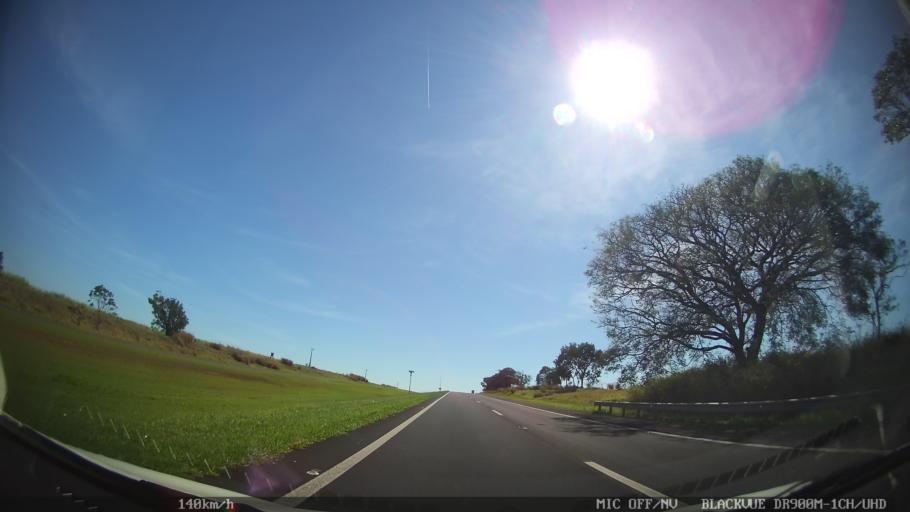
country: BR
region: Sao Paulo
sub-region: Santa Rita Do Passa Quatro
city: Santa Rita do Passa Quatro
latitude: -21.6737
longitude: -47.6056
